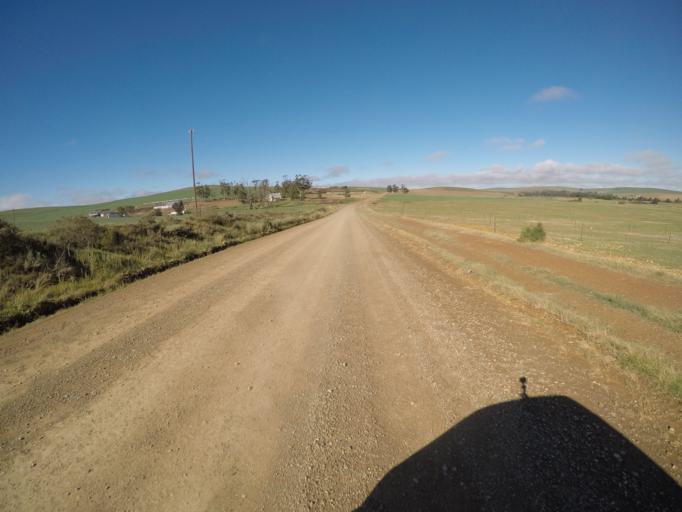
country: ZA
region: Western Cape
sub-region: Overberg District Municipality
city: Caledon
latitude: -34.1048
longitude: 19.7044
